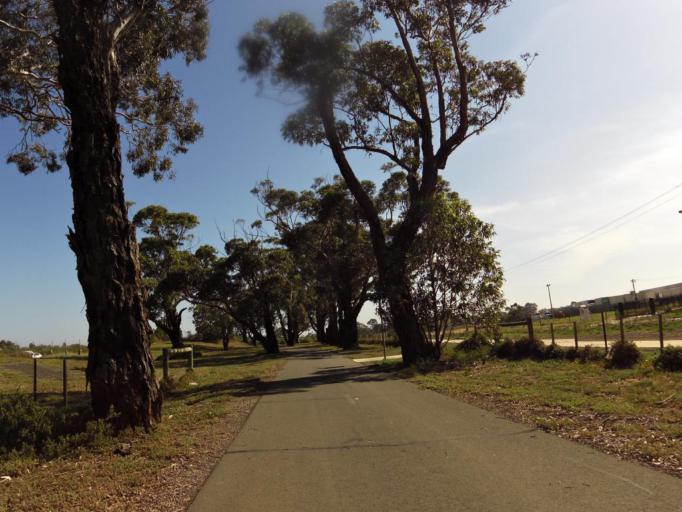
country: AU
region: Victoria
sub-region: Wyndham
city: Werribee
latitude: -37.9185
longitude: 144.6600
